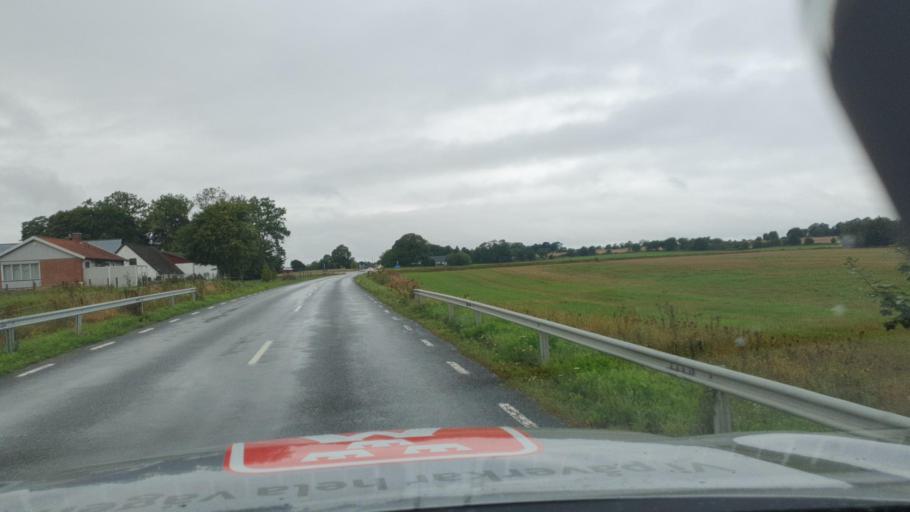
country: SE
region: Skane
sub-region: Simrishamns Kommun
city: Kivik
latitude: 55.5811
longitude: 14.1288
